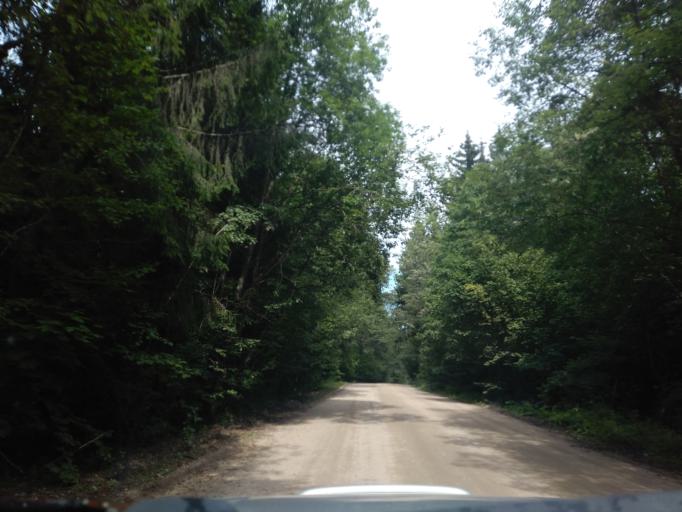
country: BY
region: Minsk
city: Khatsyezhyna
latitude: 53.8992
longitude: 27.2800
